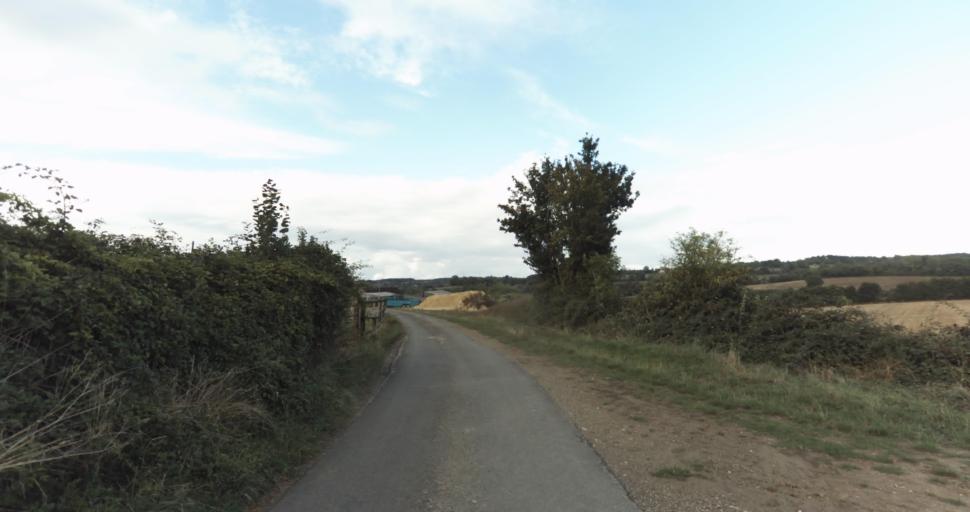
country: FR
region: Lower Normandy
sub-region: Departement de l'Orne
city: Gace
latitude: 48.7557
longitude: 0.3627
